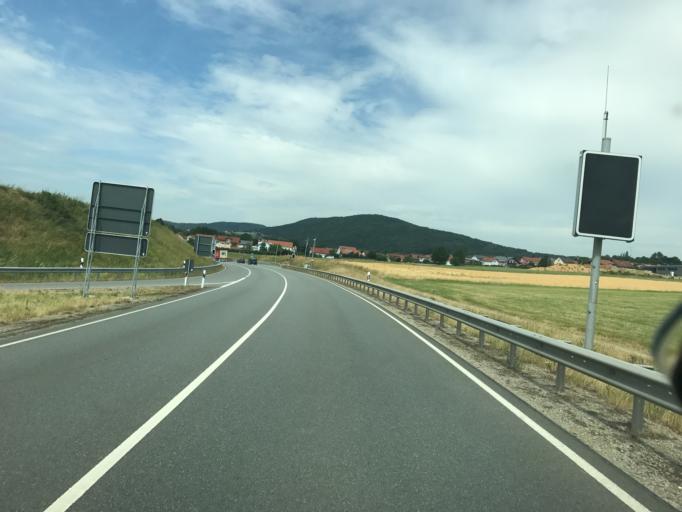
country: DE
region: Bavaria
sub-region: Upper Palatinate
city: Furth im Wald
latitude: 49.3018
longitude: 12.8521
